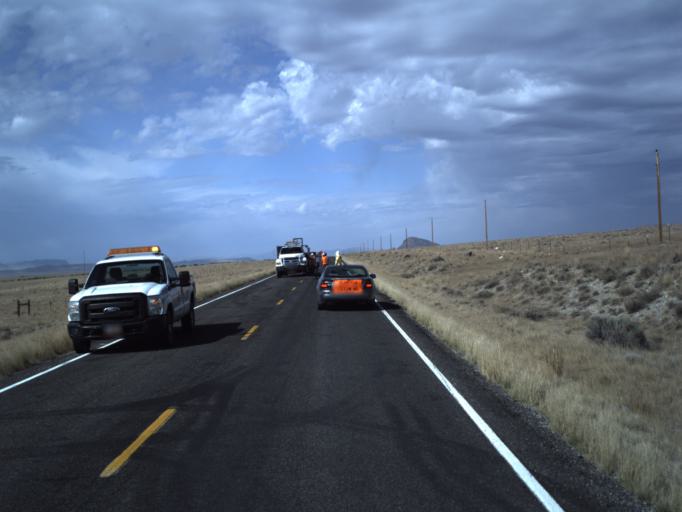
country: US
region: Utah
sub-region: Tooele County
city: Wendover
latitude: 41.4400
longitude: -113.7131
